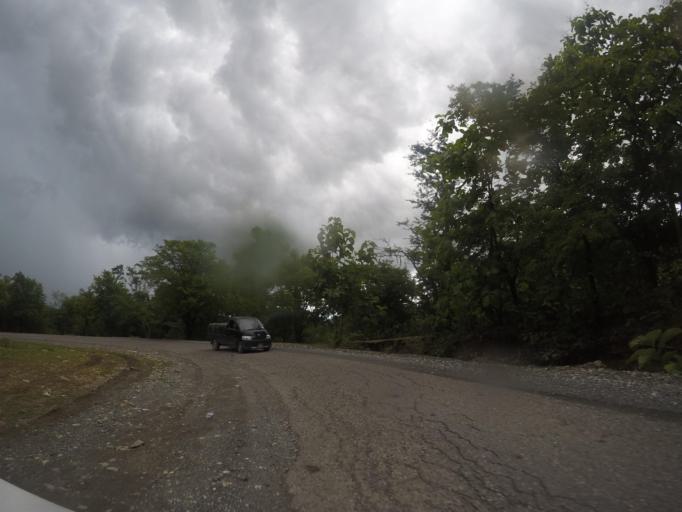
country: ID
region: East Nusa Tenggara
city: Atambua
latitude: -8.9682
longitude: 125.0160
